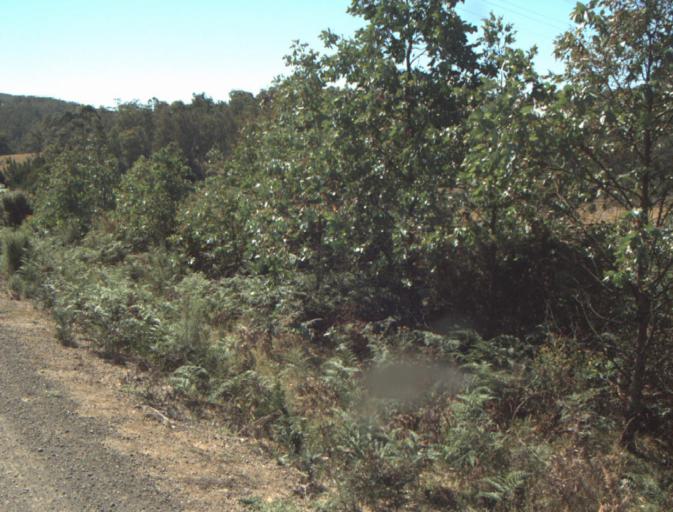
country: AU
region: Tasmania
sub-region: Dorset
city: Scottsdale
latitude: -41.3167
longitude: 147.3821
